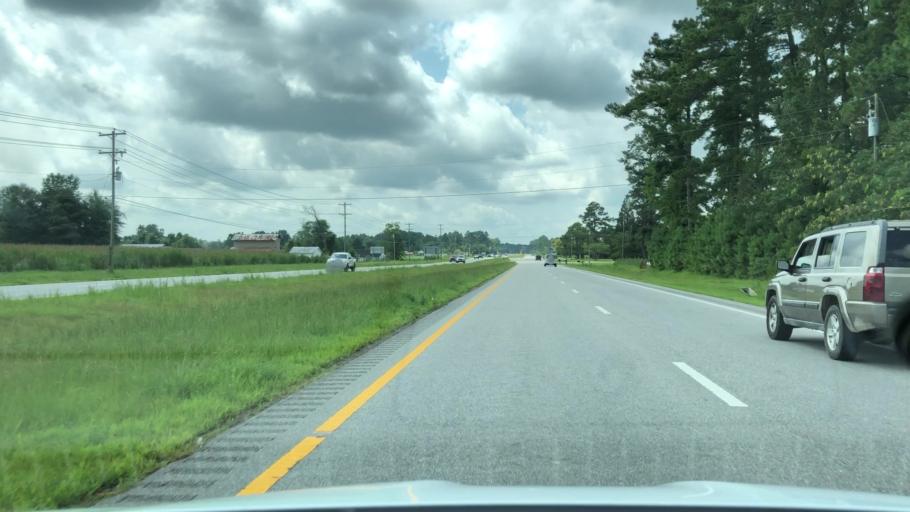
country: US
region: North Carolina
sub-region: Beaufort County
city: Washington
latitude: 35.4869
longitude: -77.1094
